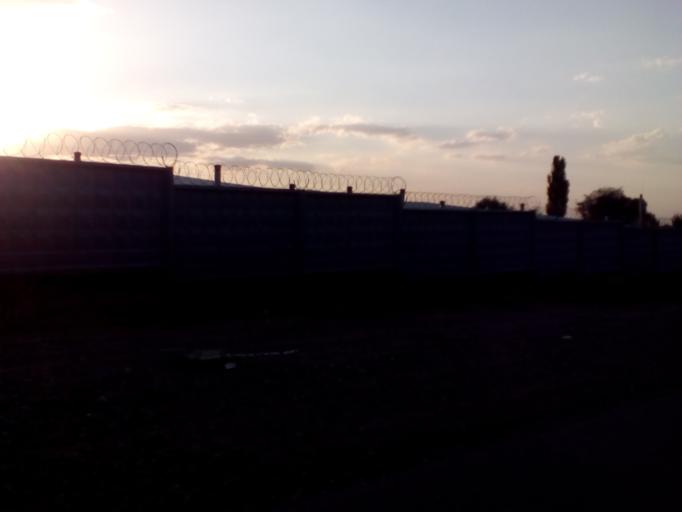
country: KZ
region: Almaty Oblysy
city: Burunday
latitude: 43.1604
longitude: 76.3823
